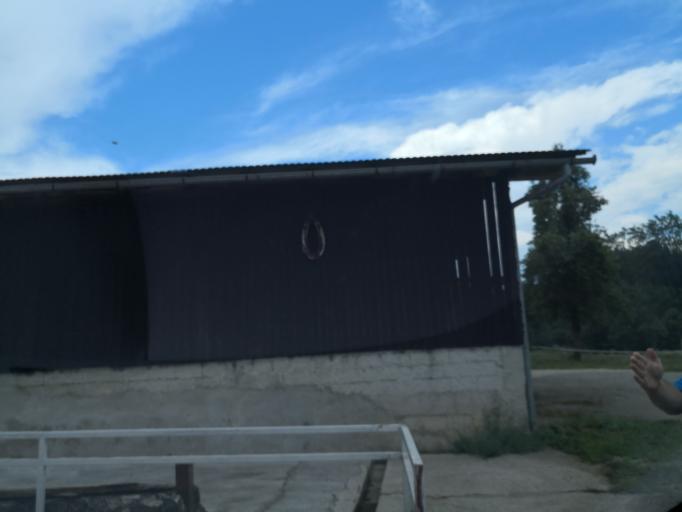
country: SI
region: Zuzemberk
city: Zuzemberk
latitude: 45.7937
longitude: 14.9773
